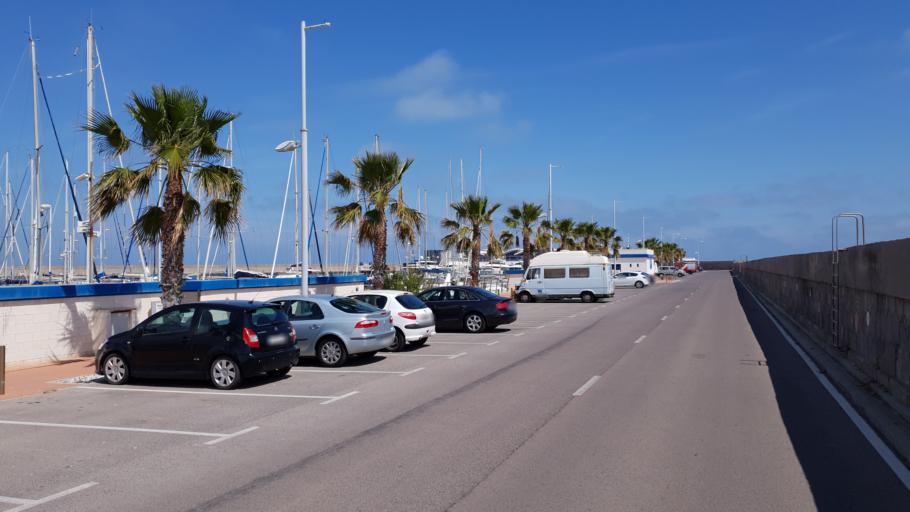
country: ES
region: Valencia
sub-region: Provincia de Castello
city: Burriana
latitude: 39.8601
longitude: -0.0726
